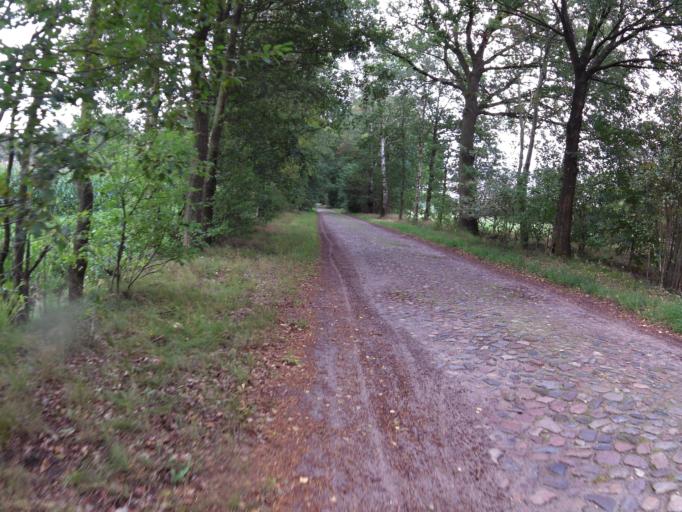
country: DE
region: Lower Saxony
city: Rotenburg
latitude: 53.1386
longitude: 9.4362
